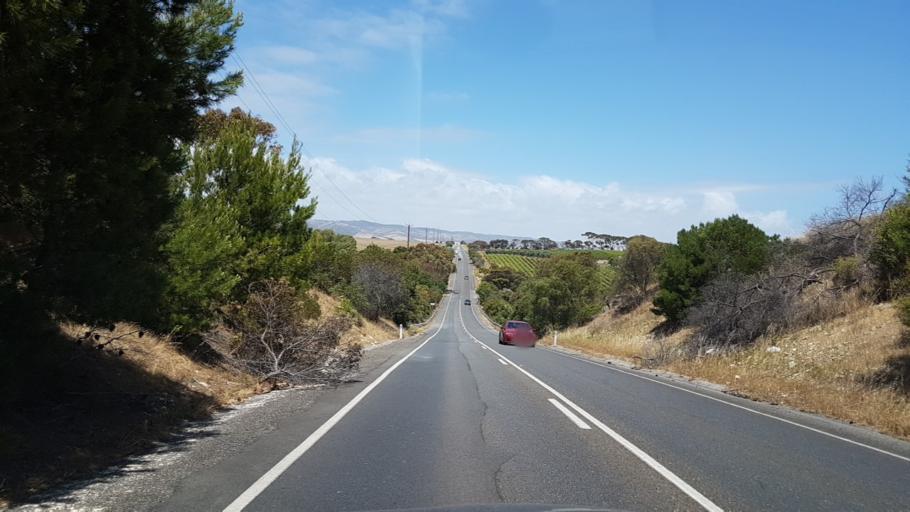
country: AU
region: South Australia
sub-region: Onkaparinga
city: Aldinga
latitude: -35.2403
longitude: 138.4813
